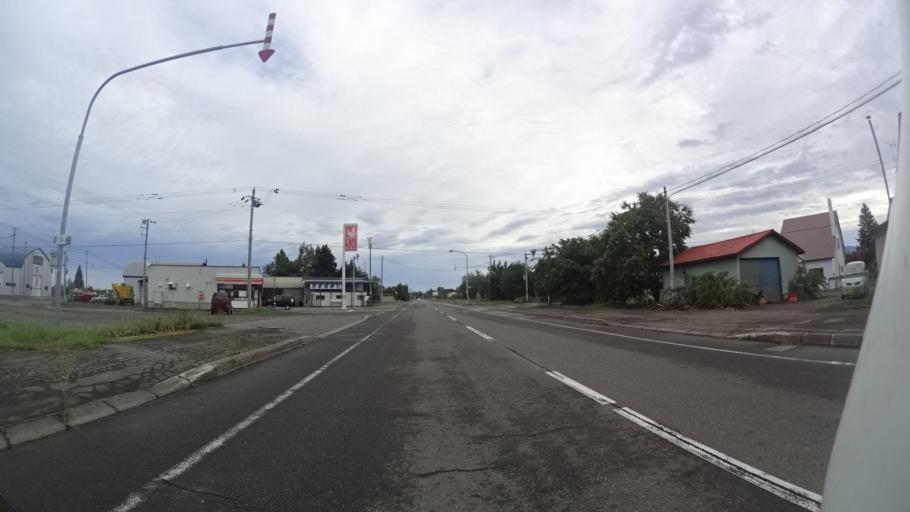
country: JP
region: Hokkaido
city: Abashiri
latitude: 43.8421
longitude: 144.5960
